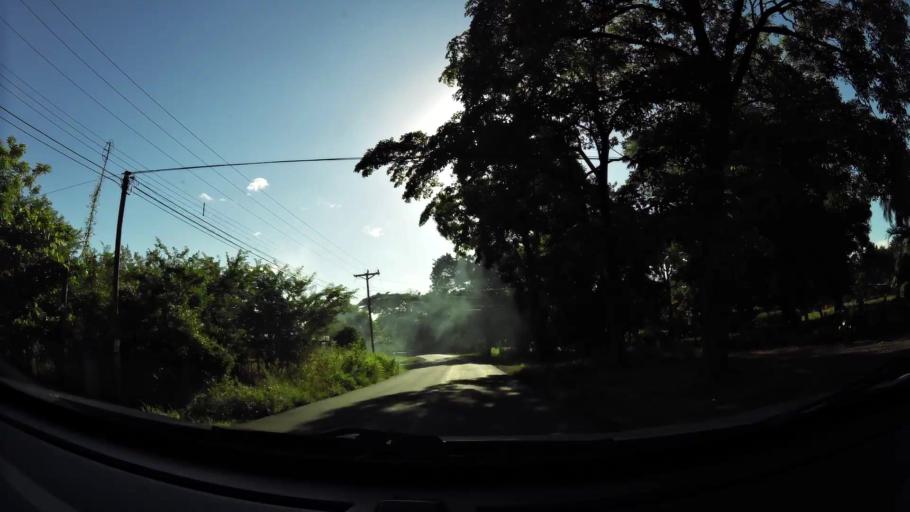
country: CR
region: Guanacaste
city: Sardinal
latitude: 10.4912
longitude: -85.6320
